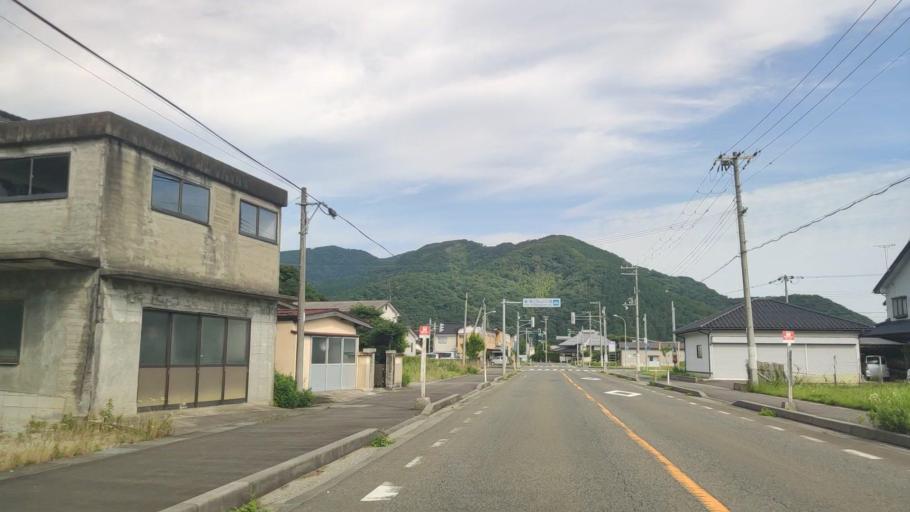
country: JP
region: Hyogo
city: Toyooka
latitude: 35.6419
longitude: 134.8338
